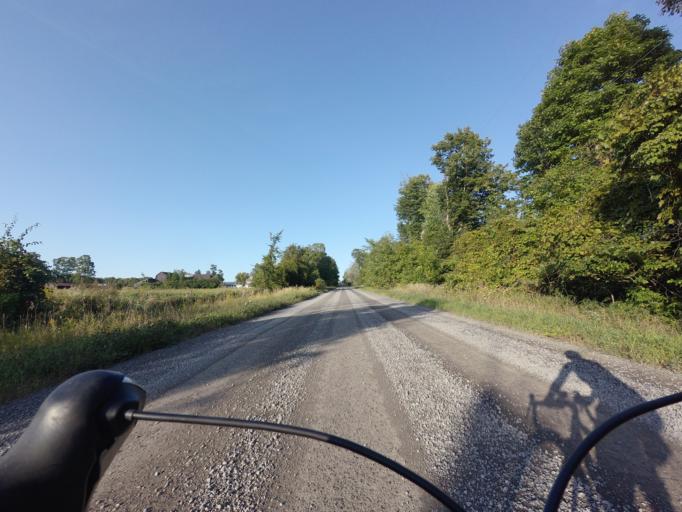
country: CA
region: Ontario
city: Bells Corners
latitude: 45.4164
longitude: -75.9536
